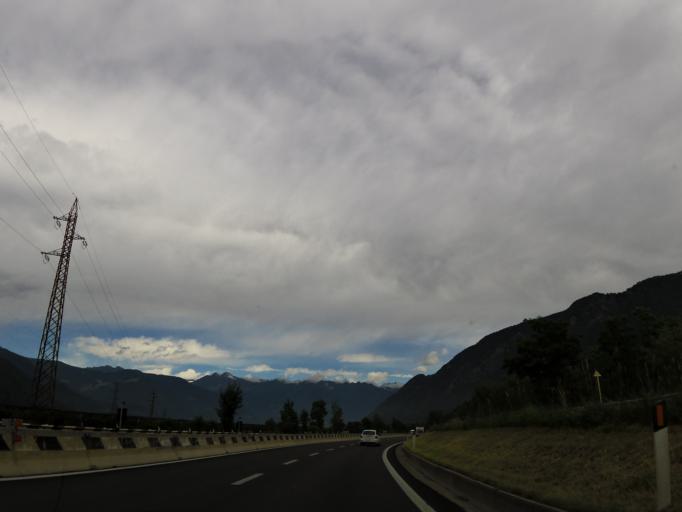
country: IT
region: Trentino-Alto Adige
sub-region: Bolzano
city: Nalles
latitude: 46.5446
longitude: 11.2241
